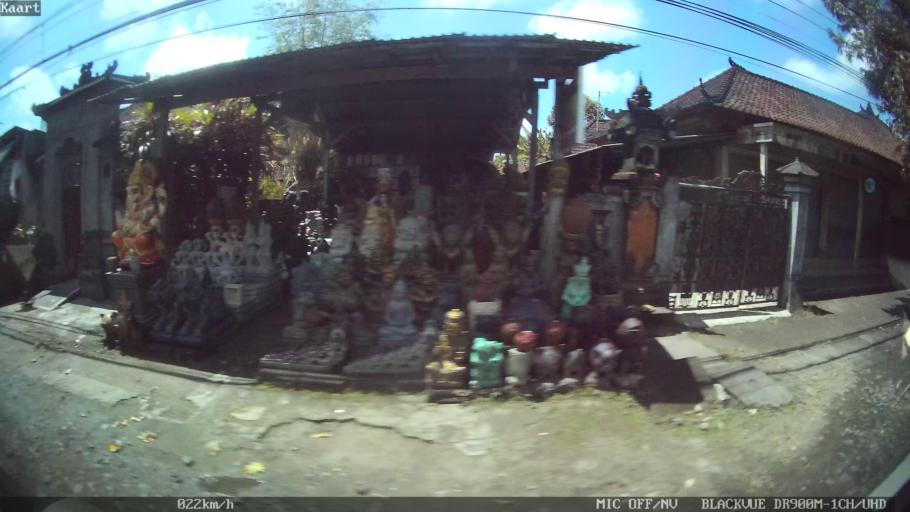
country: ID
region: Bali
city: Banjar Jabejero
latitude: -8.5933
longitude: 115.2539
